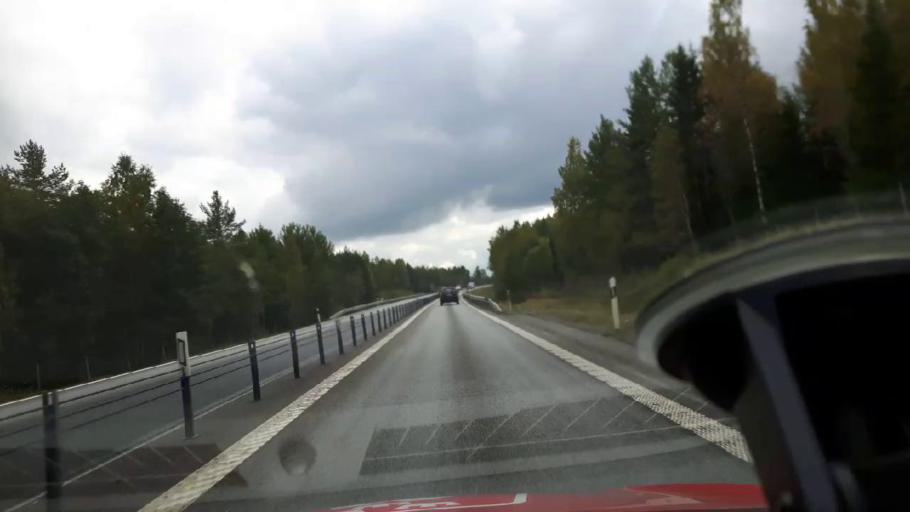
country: SE
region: Gaevleborg
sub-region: Gavle Kommun
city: Gavle
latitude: 60.7998
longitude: 17.0823
